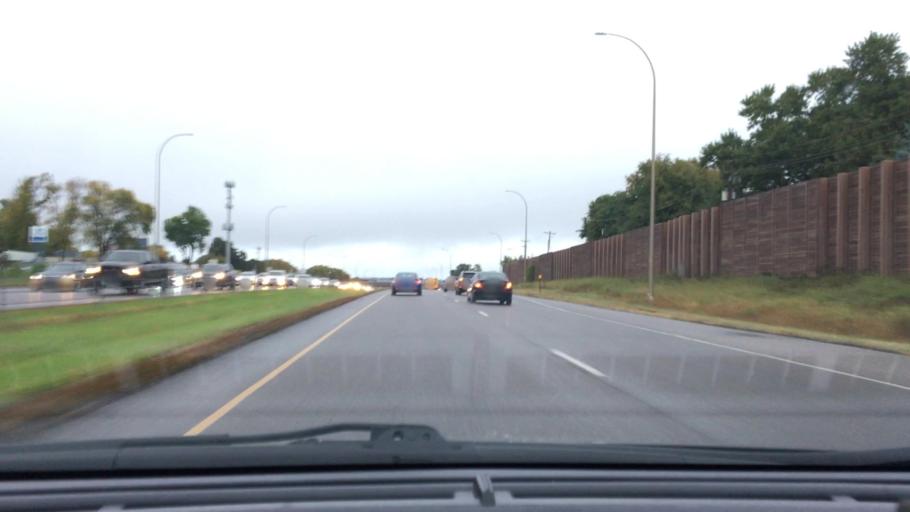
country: US
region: Minnesota
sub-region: Hennepin County
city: New Hope
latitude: 45.0180
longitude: -93.4006
